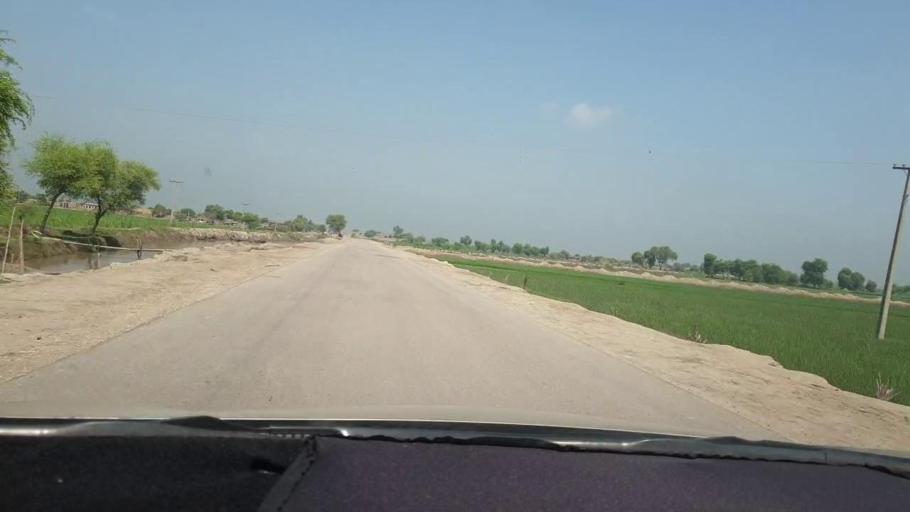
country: PK
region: Sindh
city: Miro Khan
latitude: 27.7805
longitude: 68.0542
